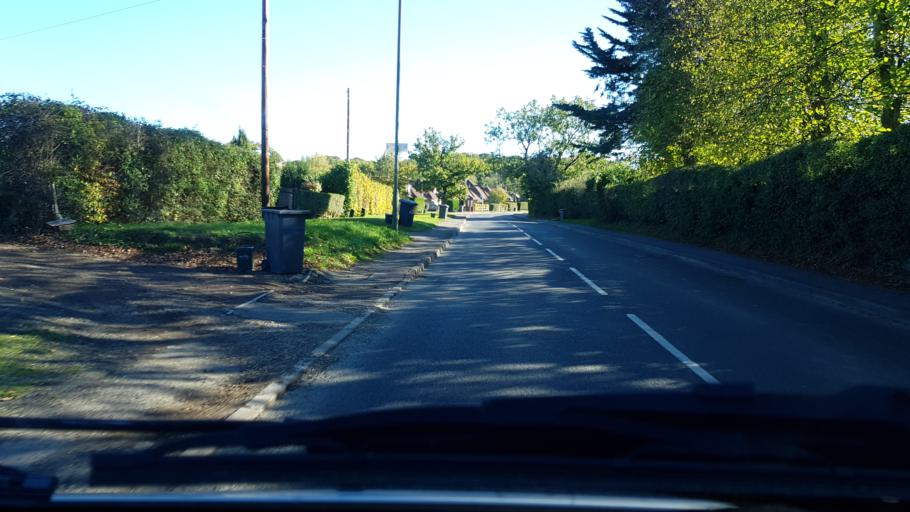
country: GB
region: England
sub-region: Surrey
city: Cranleigh
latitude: 51.1458
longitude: -0.4697
